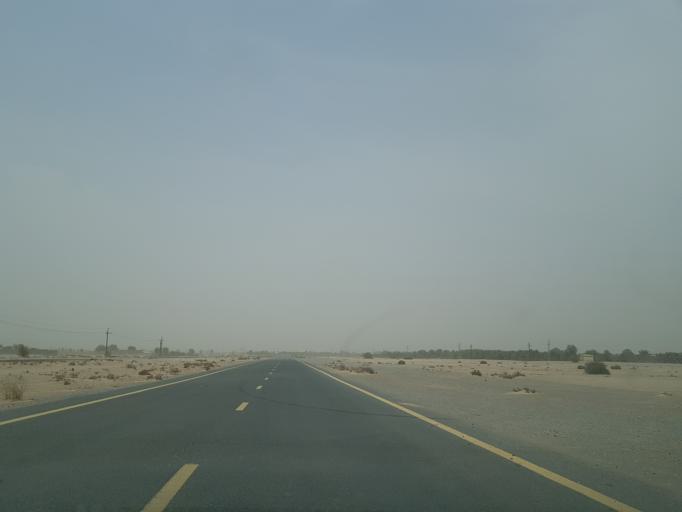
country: AE
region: Dubai
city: Dubai
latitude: 24.9371
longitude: 55.4747
